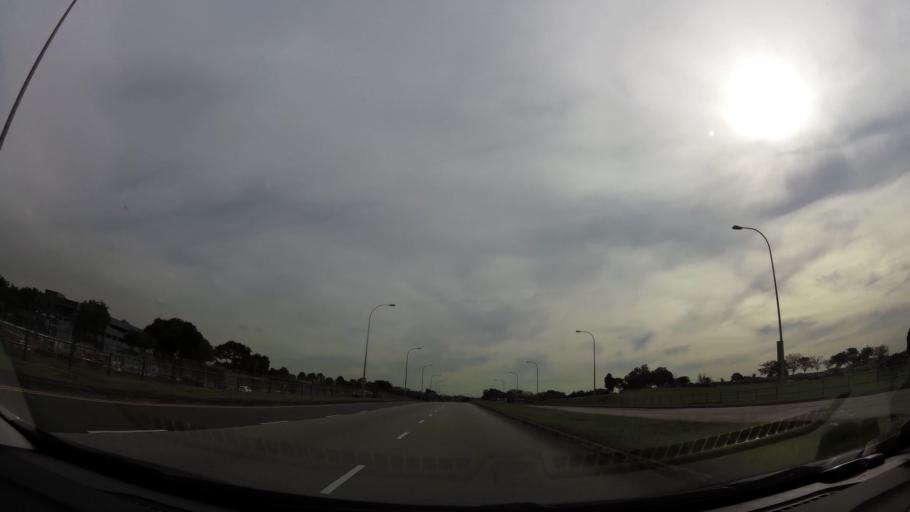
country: MY
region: Johor
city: Johor Bahru
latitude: 1.3769
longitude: 103.6960
